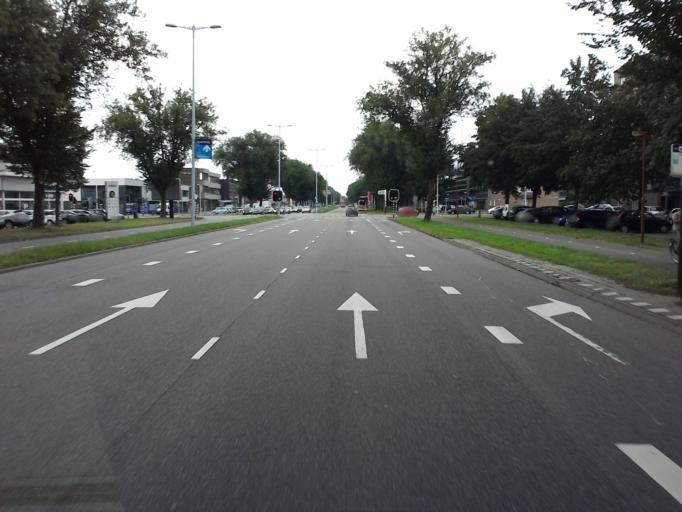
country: NL
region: Utrecht
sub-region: Gemeente Utrecht
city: Utrecht
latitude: 52.1222
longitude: 5.0889
